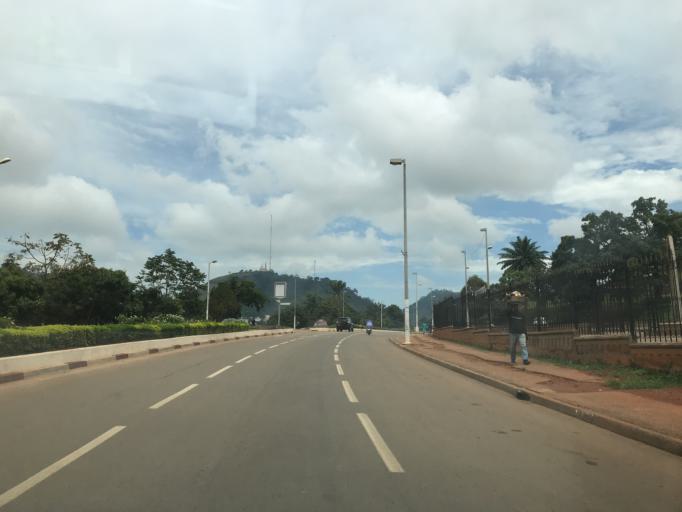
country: CM
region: Centre
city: Yaounde
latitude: 3.8883
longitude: 11.4998
